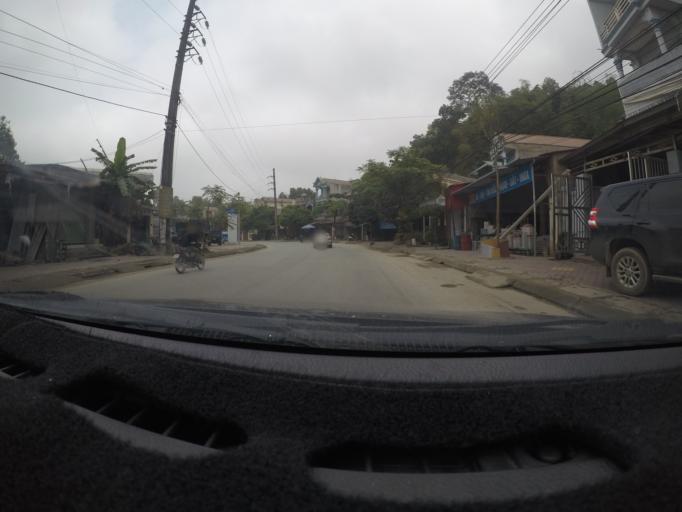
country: VN
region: Yen Bai
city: Yen Bai
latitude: 21.7355
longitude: 104.9510
